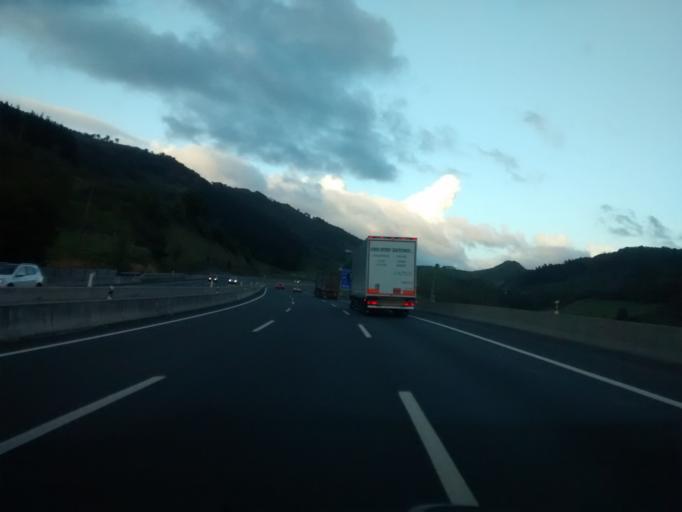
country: ES
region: Basque Country
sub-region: Provincia de Guipuzcoa
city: Orio
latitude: 43.2853
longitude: -2.0970
